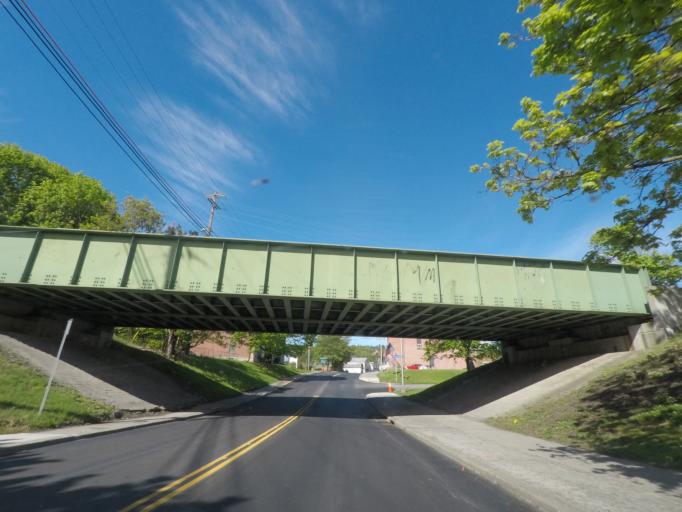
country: US
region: New York
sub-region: Albany County
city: Ravena
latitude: 42.4721
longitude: -73.8088
